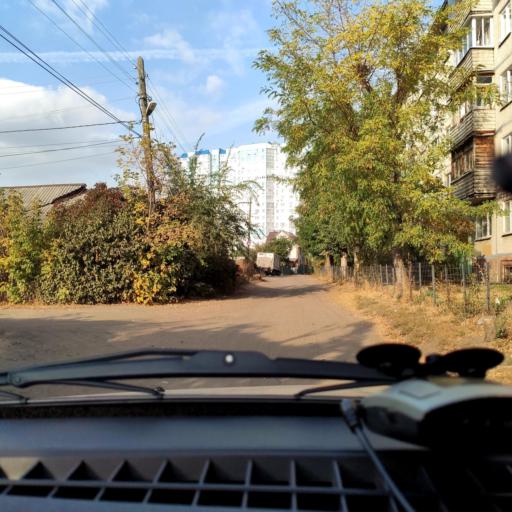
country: RU
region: Voronezj
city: Voronezh
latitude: 51.6517
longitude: 39.2372
